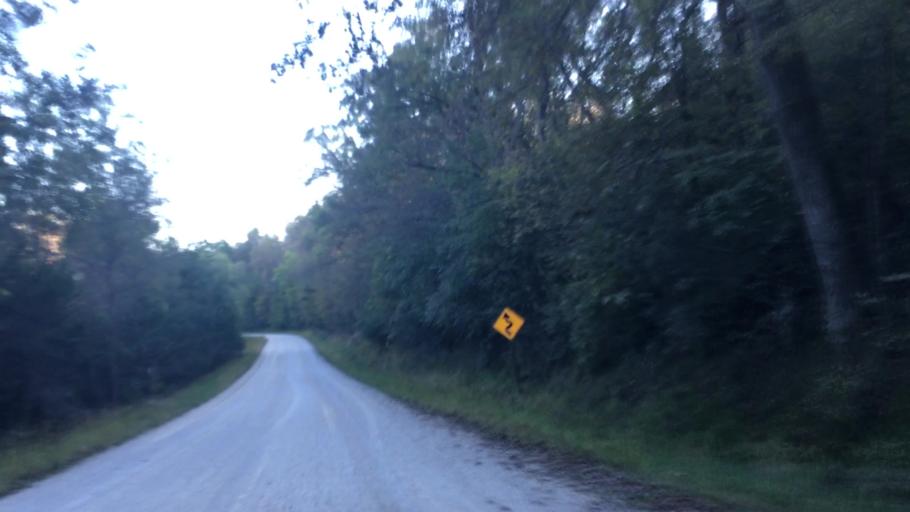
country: US
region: Minnesota
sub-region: Fillmore County
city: Preston
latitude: 43.7845
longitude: -92.0388
